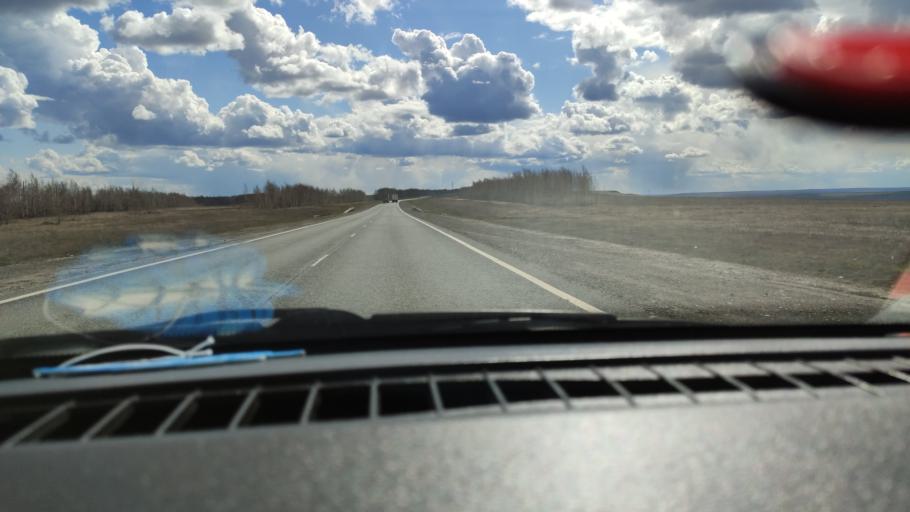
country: RU
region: Saratov
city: Dukhovnitskoye
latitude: 52.8502
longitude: 48.2563
